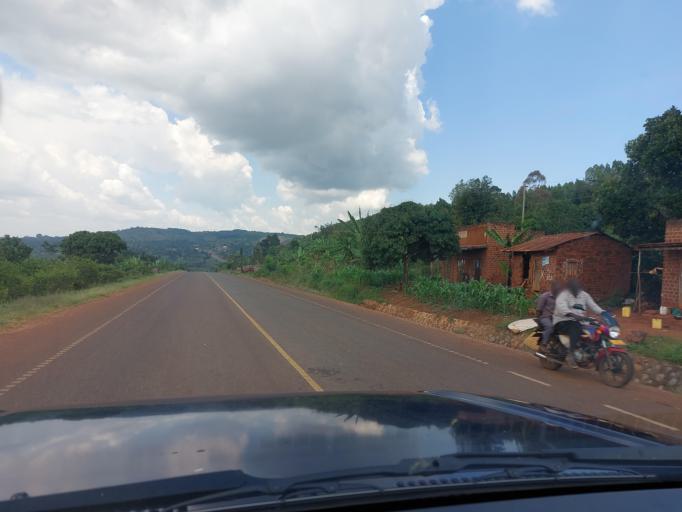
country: UG
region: Central Region
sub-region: Buikwe District
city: Njeru
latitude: 0.3349
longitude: 33.1227
